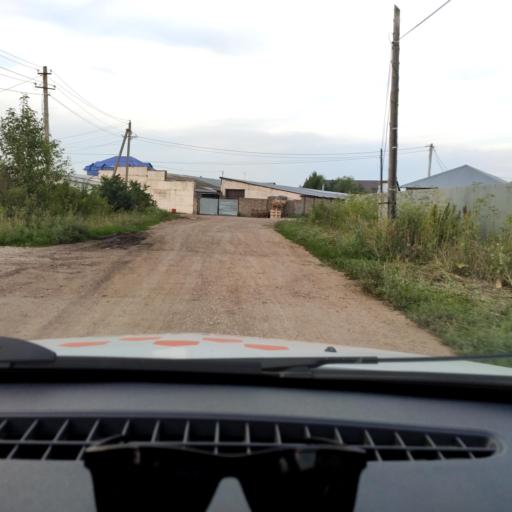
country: RU
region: Bashkortostan
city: Ufa
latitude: 54.6129
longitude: 55.9324
